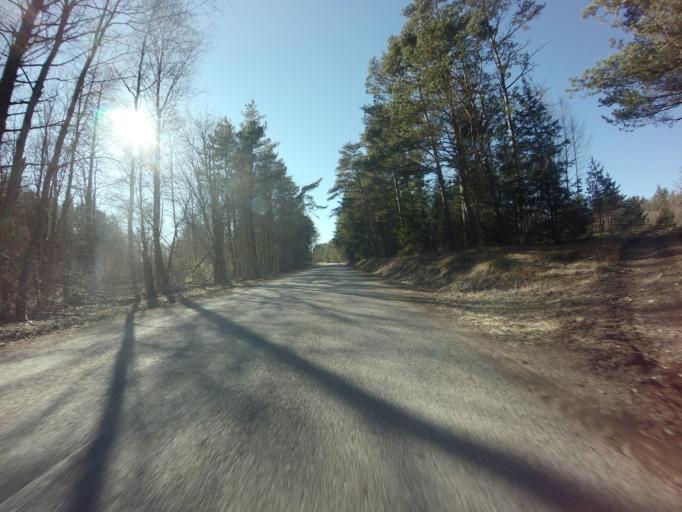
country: EE
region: Saare
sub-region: Kuressaare linn
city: Kuressaare
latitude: 58.5704
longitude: 22.4949
